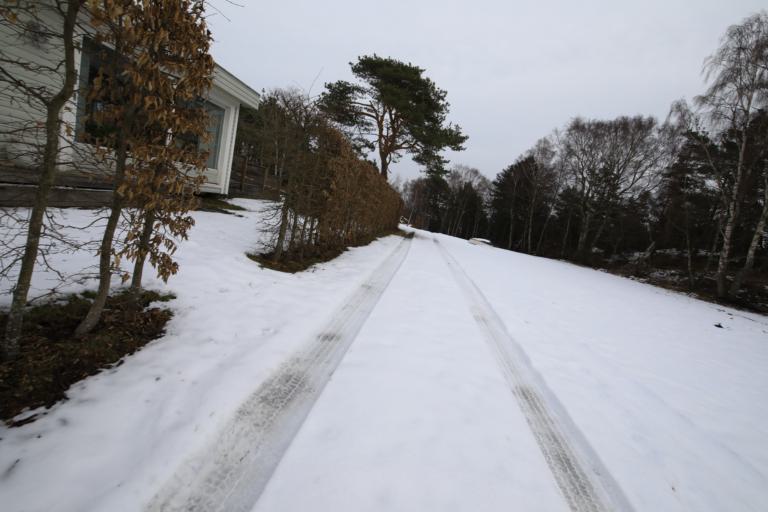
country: SE
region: Halland
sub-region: Kungsbacka Kommun
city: Frillesas
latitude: 57.2160
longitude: 12.1503
